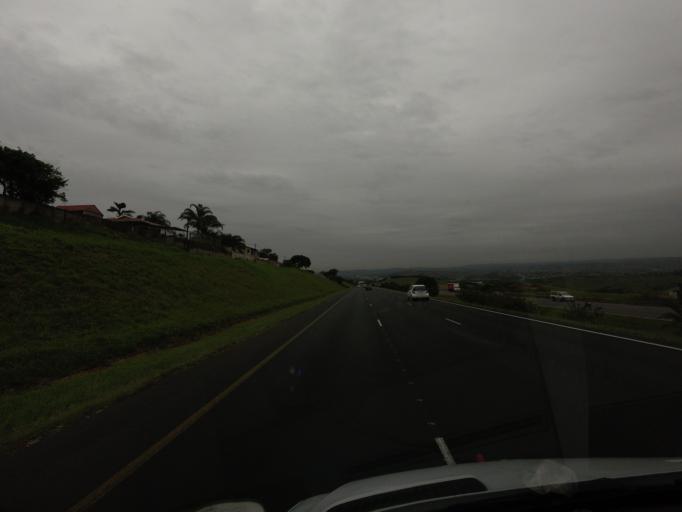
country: ZA
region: KwaZulu-Natal
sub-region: eThekwini Metropolitan Municipality
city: Durban
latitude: -29.7402
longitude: 31.0465
